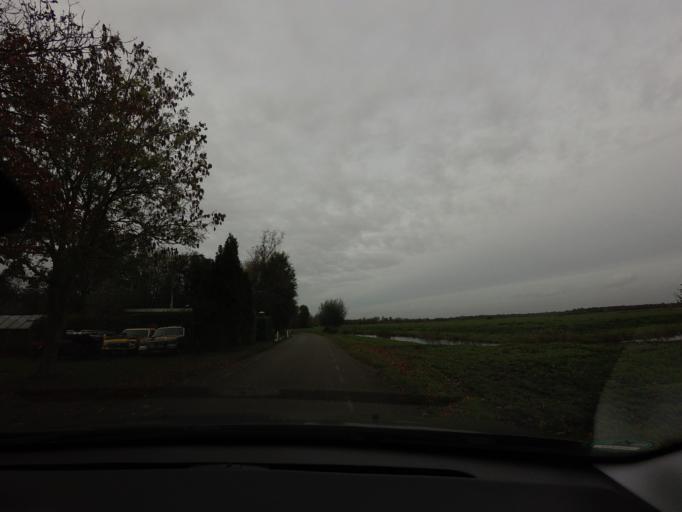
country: NL
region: Overijssel
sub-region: Gemeente Steenwijkerland
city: Oldemarkt
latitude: 52.7763
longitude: 5.9838
